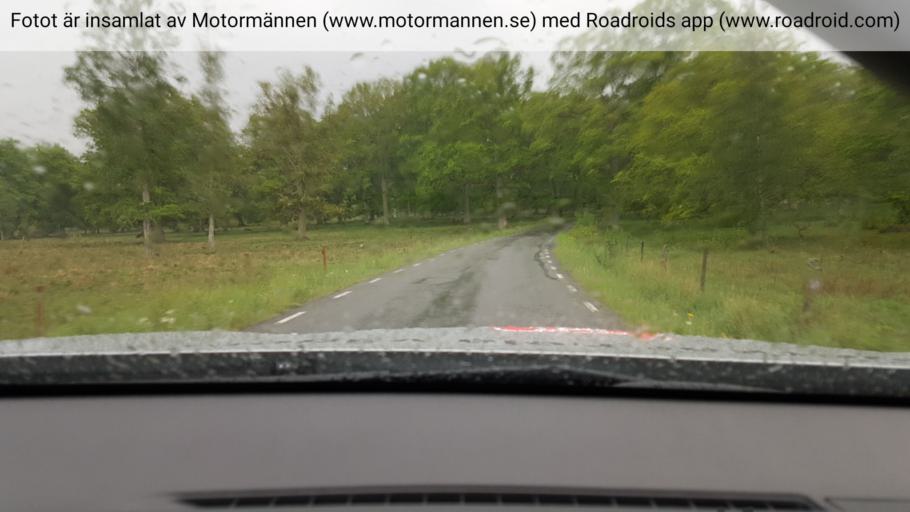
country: SE
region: Vaestra Goetaland
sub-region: Skara Kommun
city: Axvall
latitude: 58.3752
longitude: 13.5684
